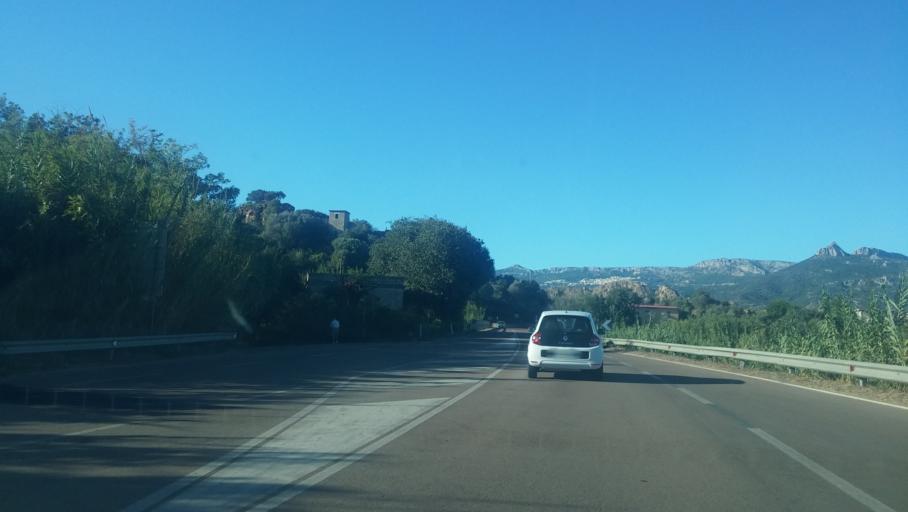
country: IT
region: Sardinia
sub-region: Provincia di Ogliastra
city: Lotzorai
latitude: 39.9622
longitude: 9.6574
